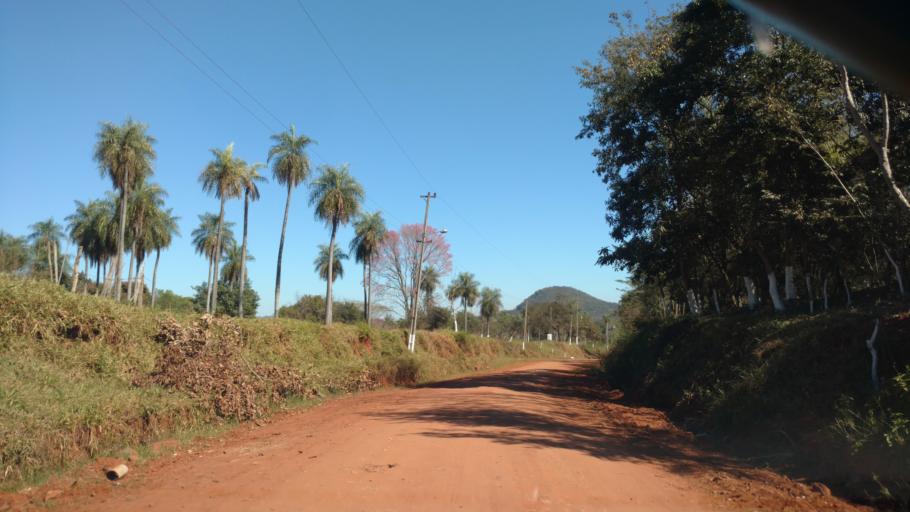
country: PY
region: Paraguari
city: Yaguaron
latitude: -25.5647
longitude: -57.3058
